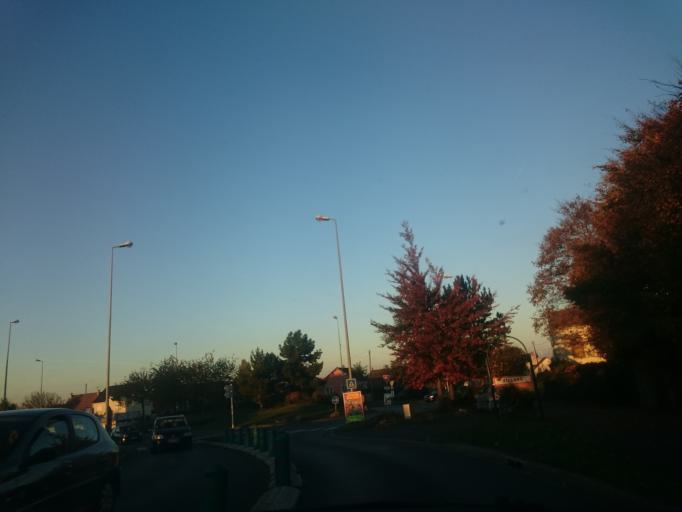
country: FR
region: Ile-de-France
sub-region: Departement de l'Essonne
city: Villabe
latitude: 48.5878
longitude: 2.4512
